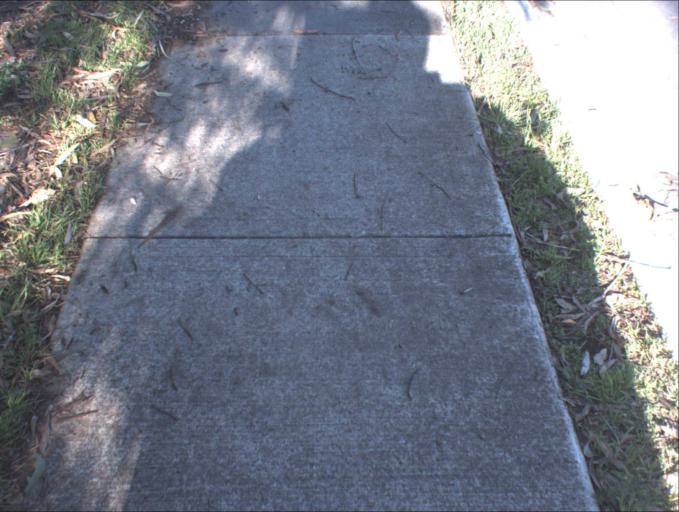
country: AU
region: Queensland
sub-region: Logan
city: Chambers Flat
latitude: -27.7656
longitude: 153.1078
